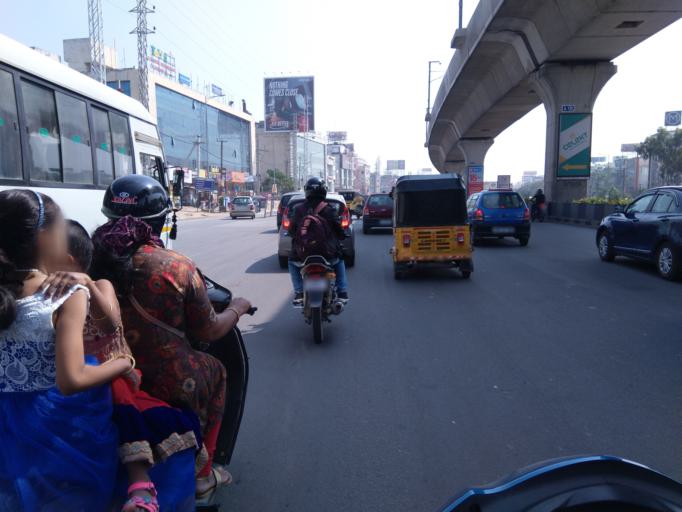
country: IN
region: Telangana
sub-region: Rangareddi
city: Kukatpalli
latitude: 17.4961
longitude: 78.3967
